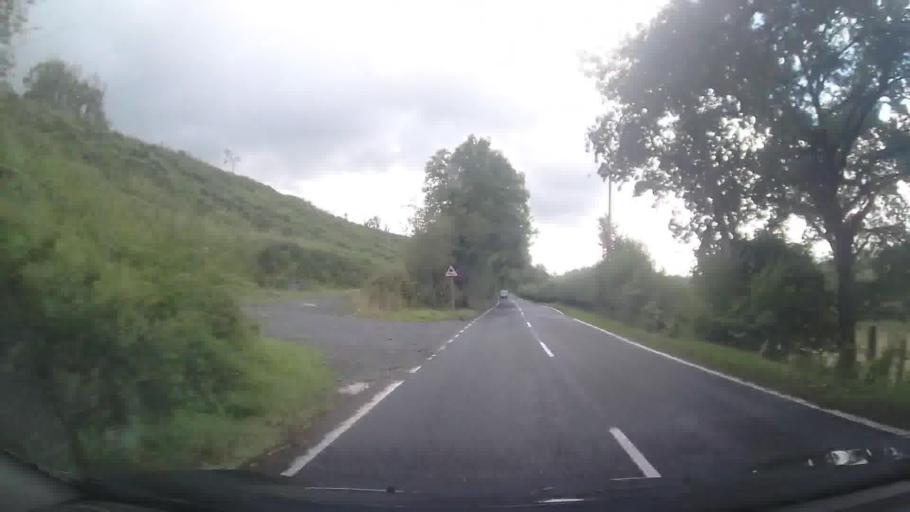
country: GB
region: Wales
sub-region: Carmarthenshire
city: Llandovery
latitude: 52.0531
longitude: -3.7237
